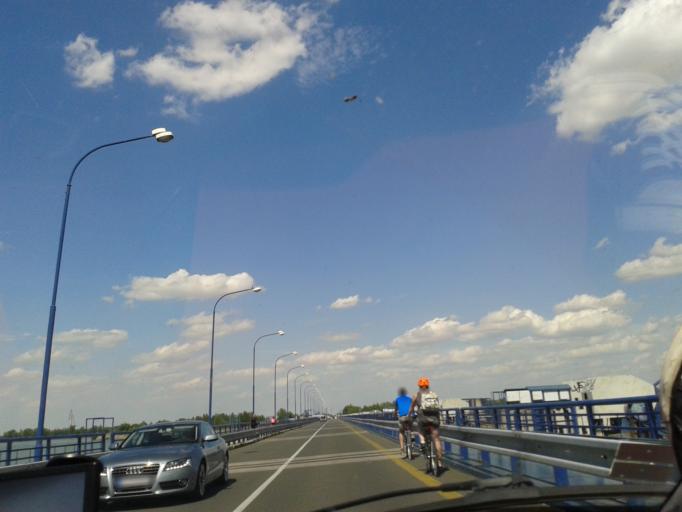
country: HU
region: Gyor-Moson-Sopron
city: Rajka
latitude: 48.0263
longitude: 17.2184
